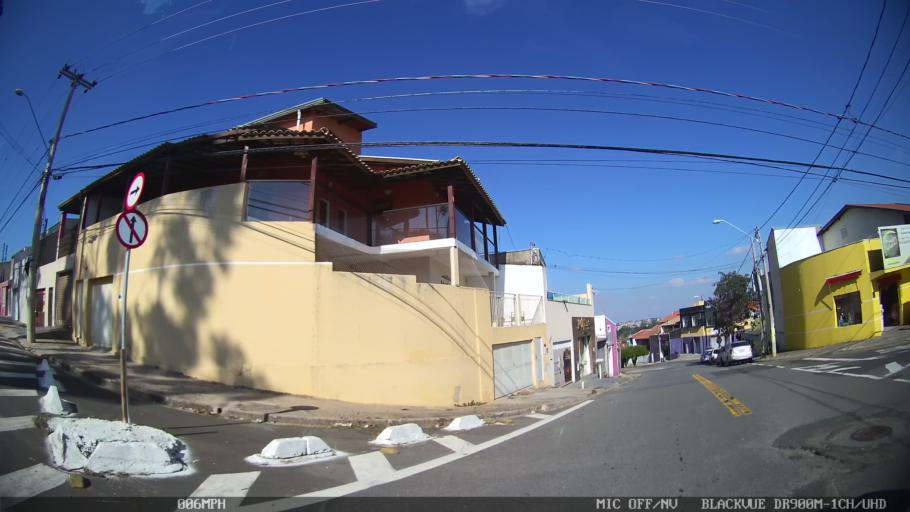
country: BR
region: Sao Paulo
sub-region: Campinas
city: Campinas
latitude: -22.9460
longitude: -47.1209
